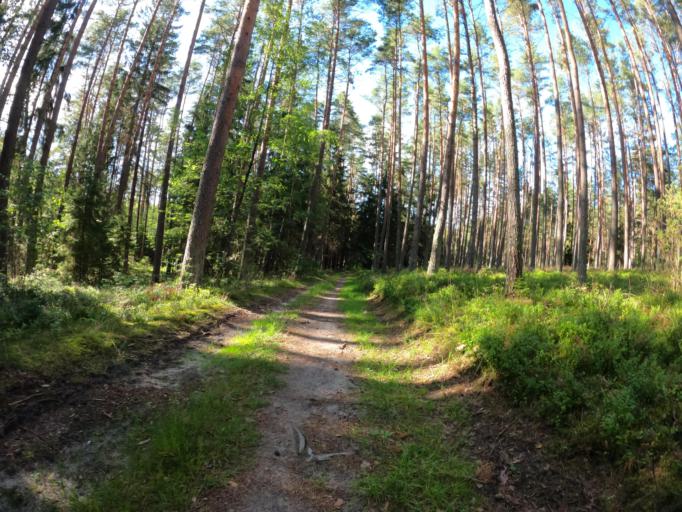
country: PL
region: West Pomeranian Voivodeship
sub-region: Powiat bialogardzki
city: Tychowo
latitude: 54.0538
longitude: 16.3067
